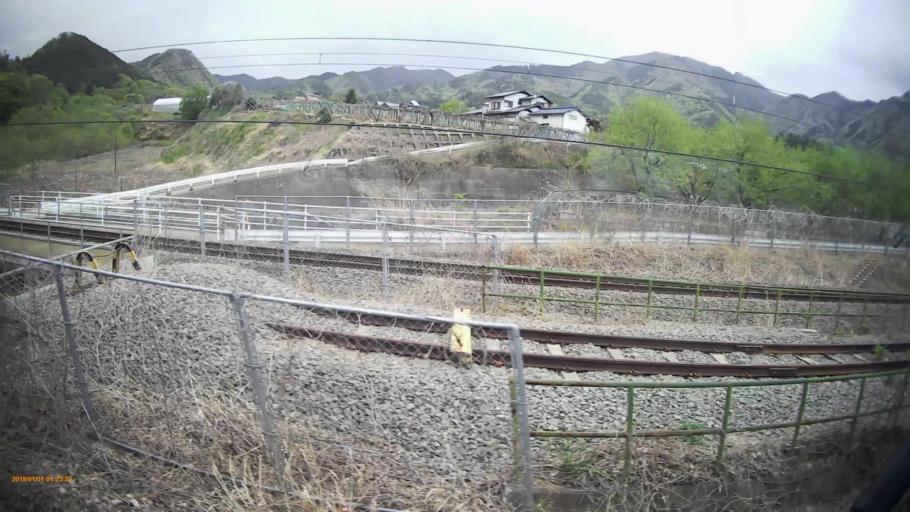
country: JP
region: Yamanashi
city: Enzan
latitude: 35.6813
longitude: 138.7411
